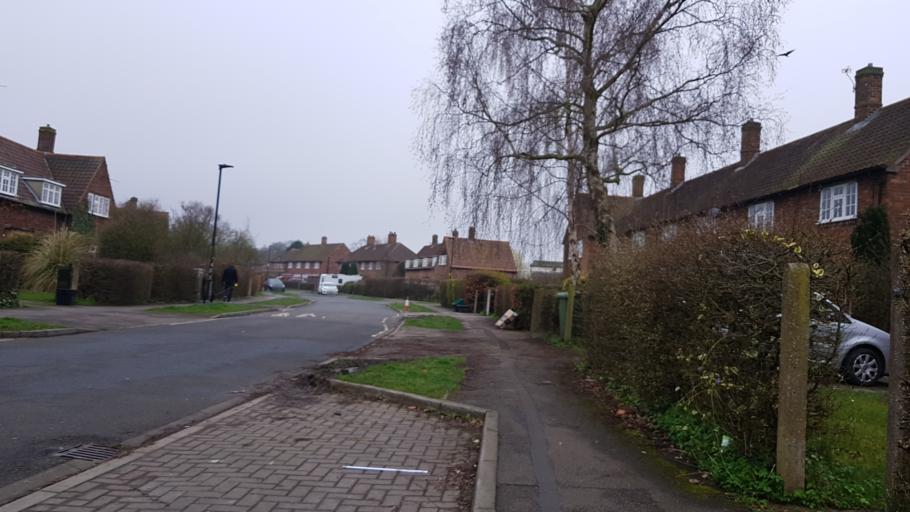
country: GB
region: England
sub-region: City of York
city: Haxby
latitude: 53.9892
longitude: -1.0769
